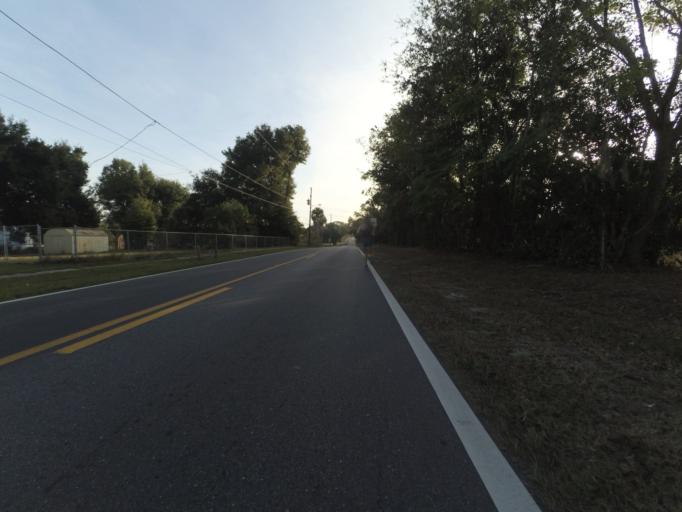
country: US
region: Florida
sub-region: Lake County
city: Umatilla
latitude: 28.9311
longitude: -81.6734
